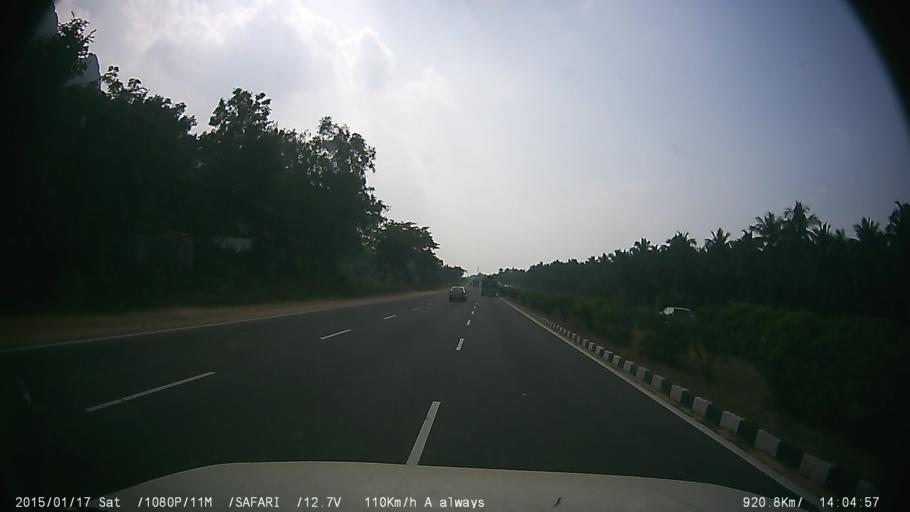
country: IN
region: Tamil Nadu
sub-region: Vellore
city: Odugattur
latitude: 12.8515
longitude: 78.8133
